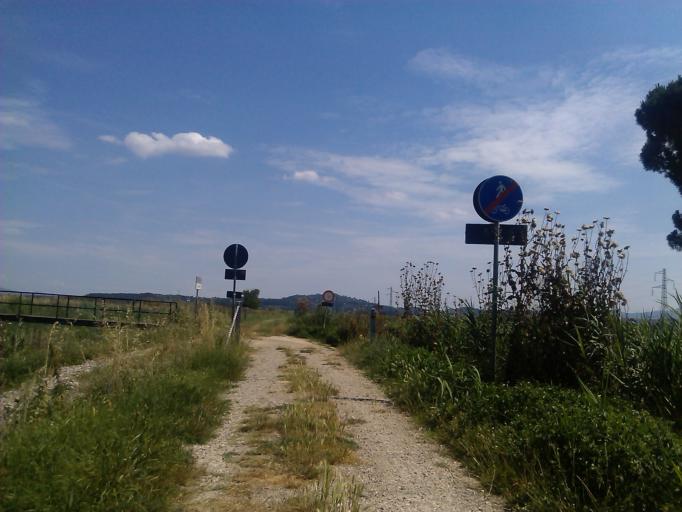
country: IT
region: Umbria
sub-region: Provincia di Perugia
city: Pozzuolo
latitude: 43.0709
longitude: 11.9200
